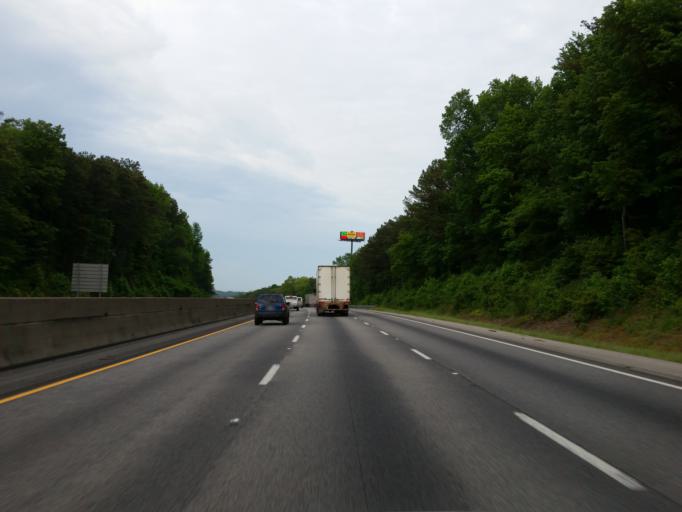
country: US
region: Alabama
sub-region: Saint Clair County
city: Moody
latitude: 33.5694
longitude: -86.5014
